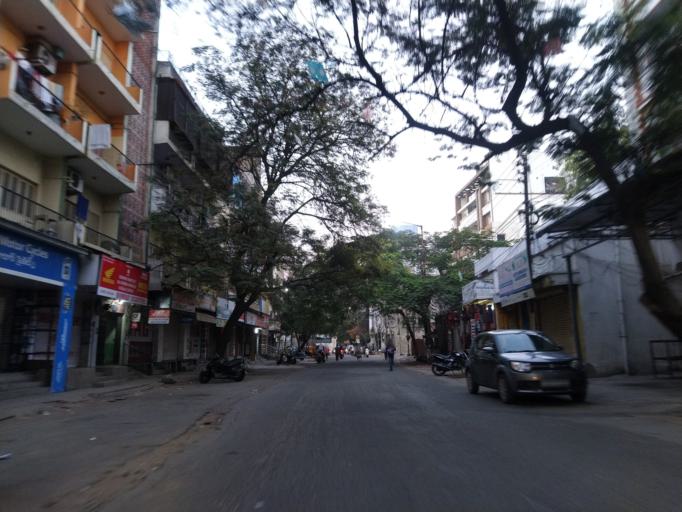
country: IN
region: Telangana
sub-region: Hyderabad
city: Hyderabad
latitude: 17.3917
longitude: 78.4860
